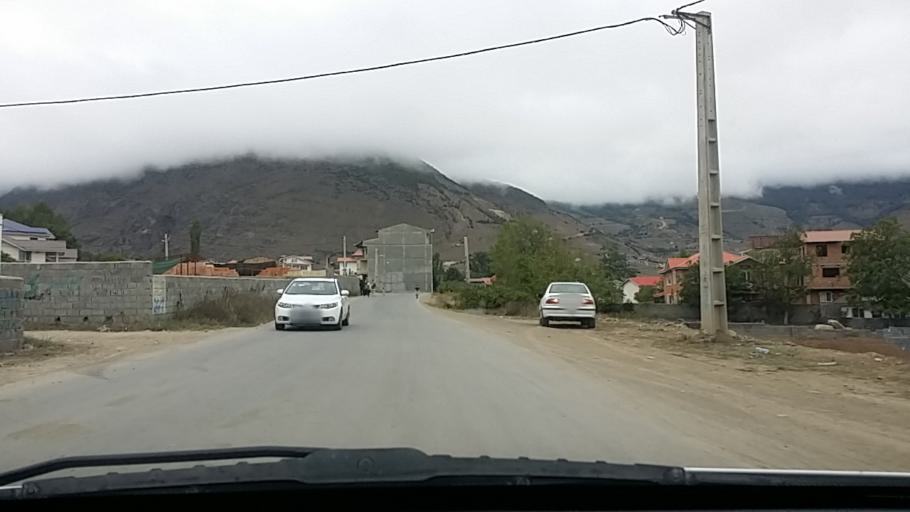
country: IR
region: Mazandaran
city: `Abbasabad
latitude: 36.4985
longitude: 51.1543
